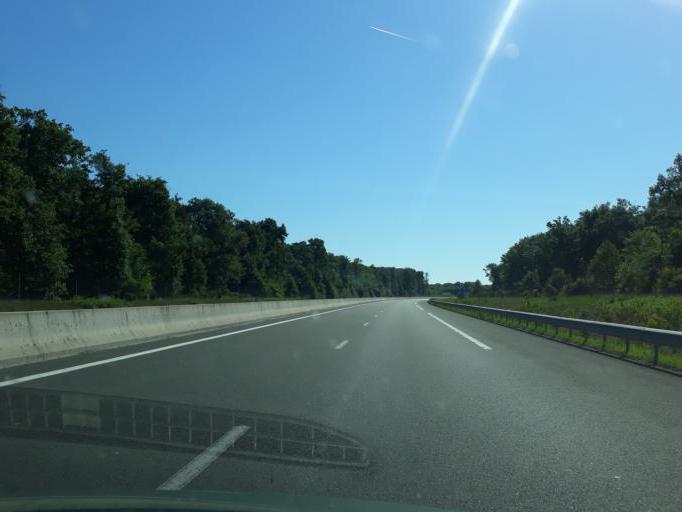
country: FR
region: Centre
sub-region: Departement du Loiret
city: Fontenay-sur-Loing
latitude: 48.0652
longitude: 2.7900
